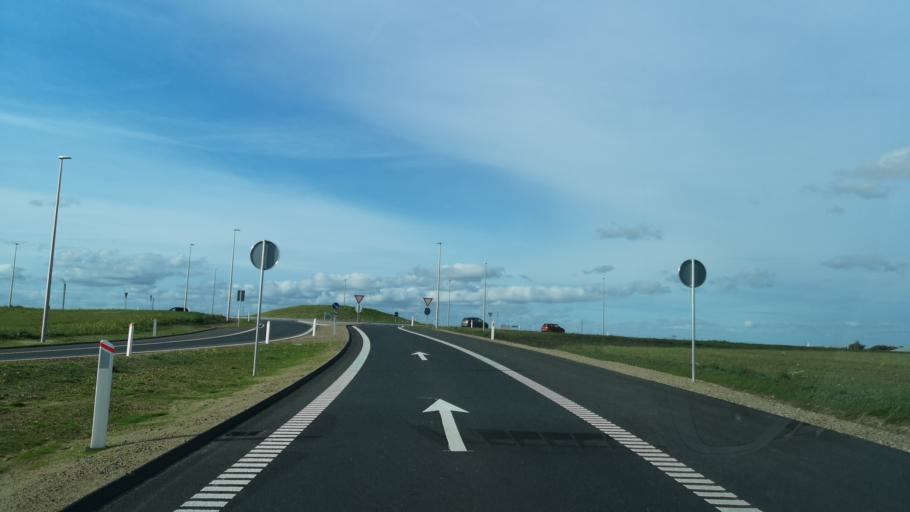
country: DK
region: Central Jutland
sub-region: Holstebro Kommune
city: Holstebro
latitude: 56.3865
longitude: 8.6565
